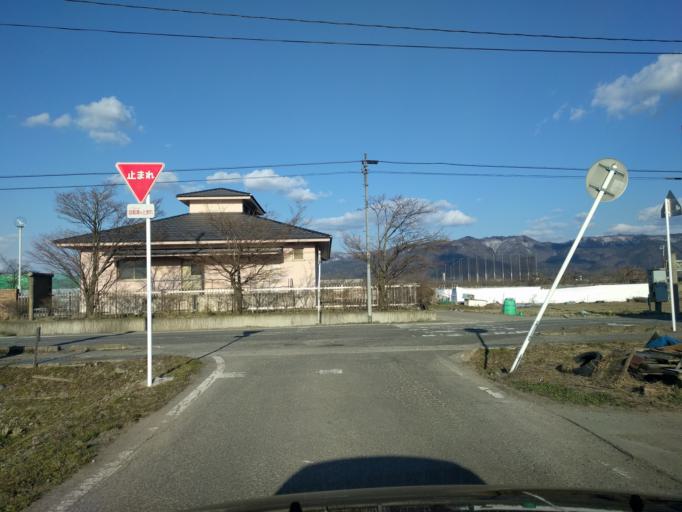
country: JP
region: Fukushima
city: Kitakata
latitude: 37.4667
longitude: 139.8970
